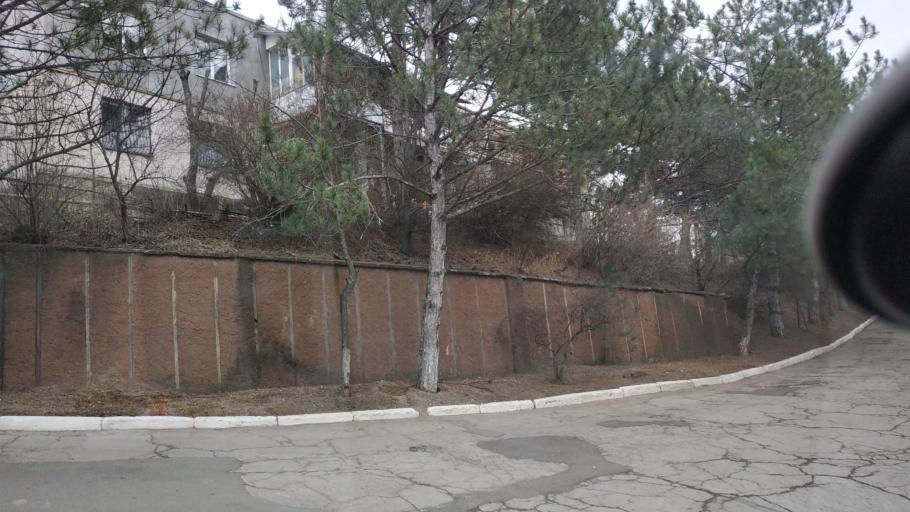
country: MD
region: Telenesti
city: Cocieri
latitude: 47.3320
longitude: 29.0846
